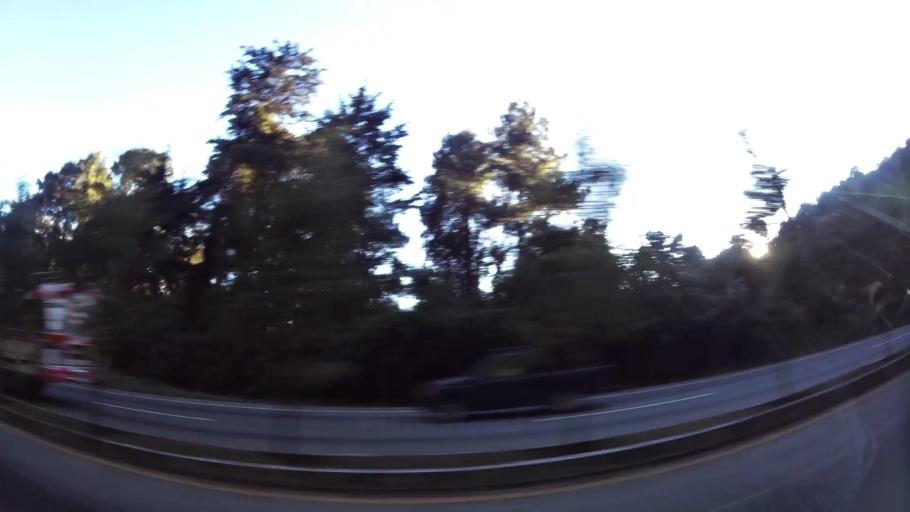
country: GT
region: Sacatepequez
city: San Lucas Sacatepequez
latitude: 14.6082
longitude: -90.6320
